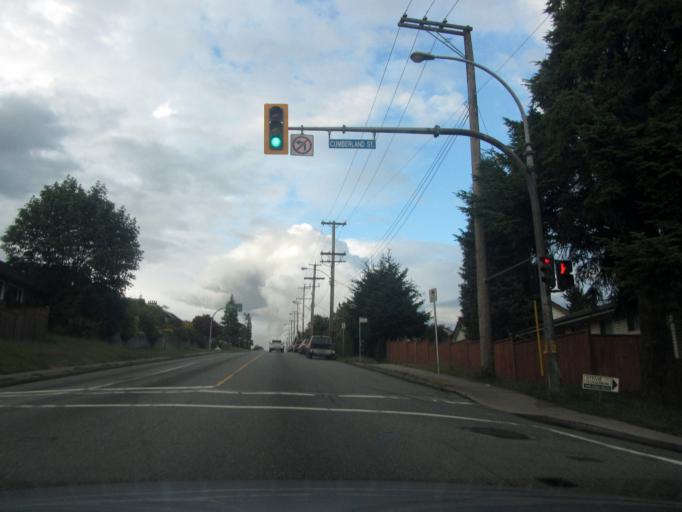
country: CA
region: British Columbia
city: New Westminster
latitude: 49.2243
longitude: -122.9084
